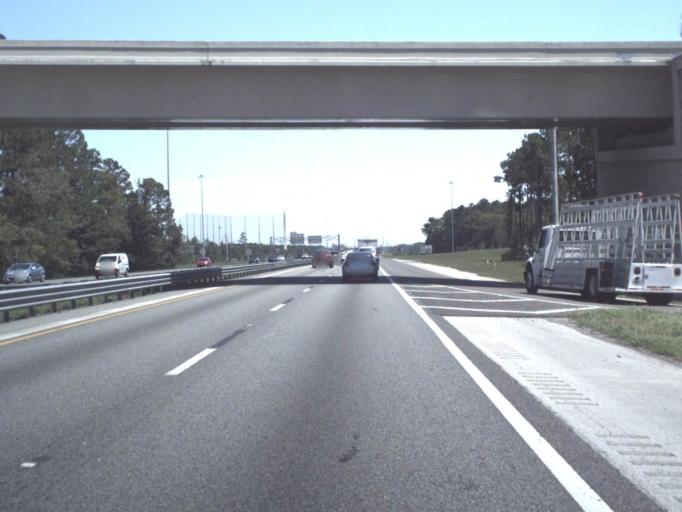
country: US
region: Florida
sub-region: Duval County
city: Jacksonville Beach
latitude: 30.2552
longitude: -81.5167
